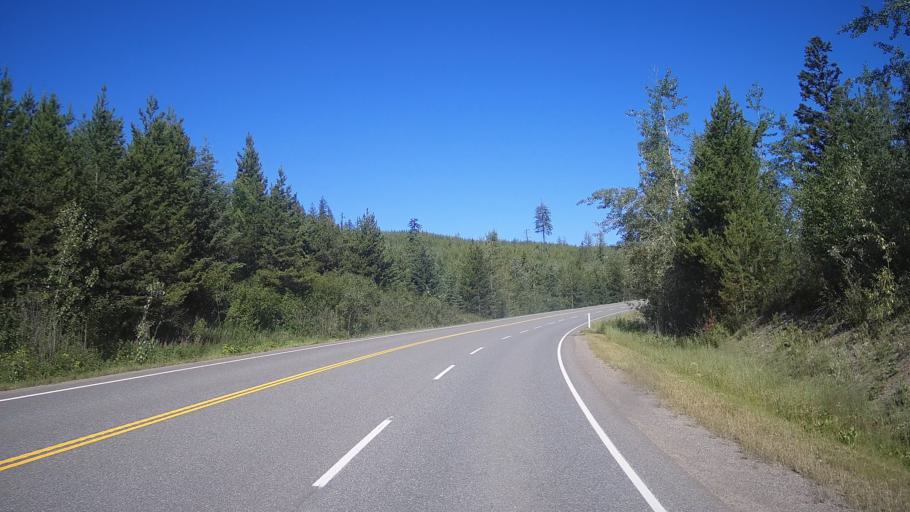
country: CA
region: British Columbia
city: Kamloops
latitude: 51.4871
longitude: -120.3203
